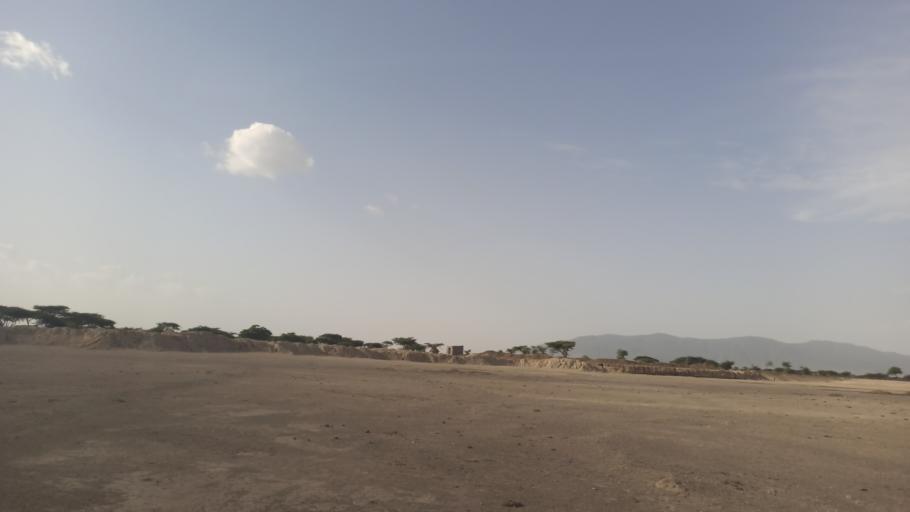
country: ET
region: Oromiya
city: Ziway
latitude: 7.6684
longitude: 38.6775
